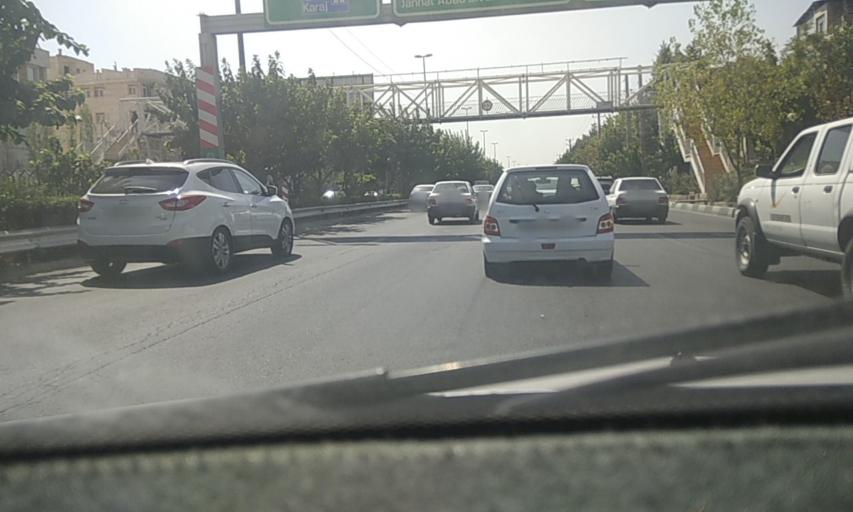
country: IR
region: Tehran
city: Tehran
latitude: 35.7533
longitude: 51.3100
